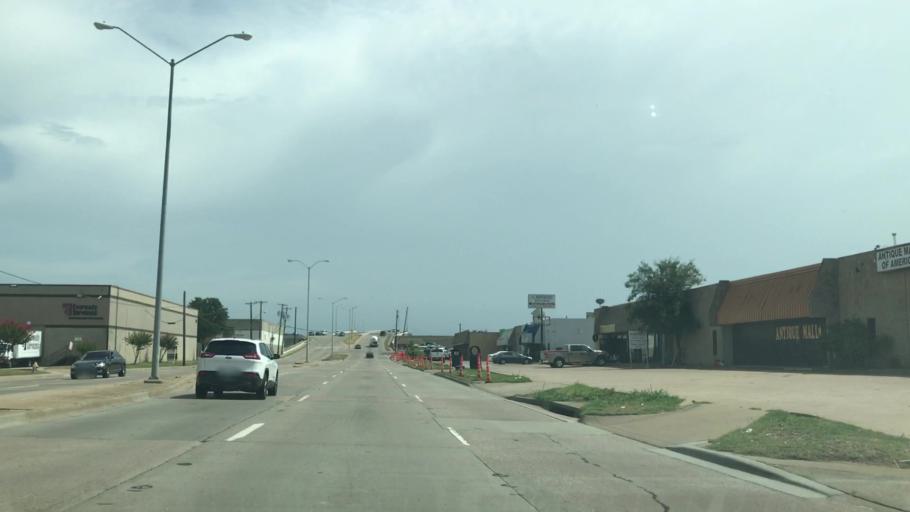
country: US
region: Texas
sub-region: Dallas County
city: Cockrell Hill
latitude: 32.8055
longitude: -96.8738
